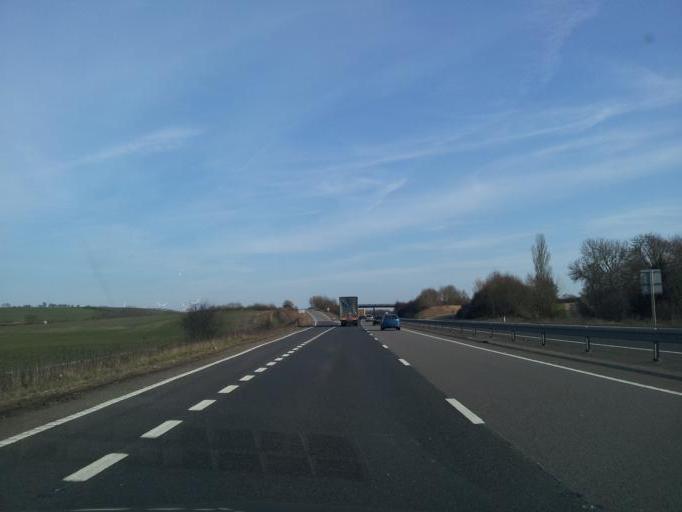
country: GB
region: England
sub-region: Bedford
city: Pertenhall
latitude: 52.3467
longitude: -0.3529
